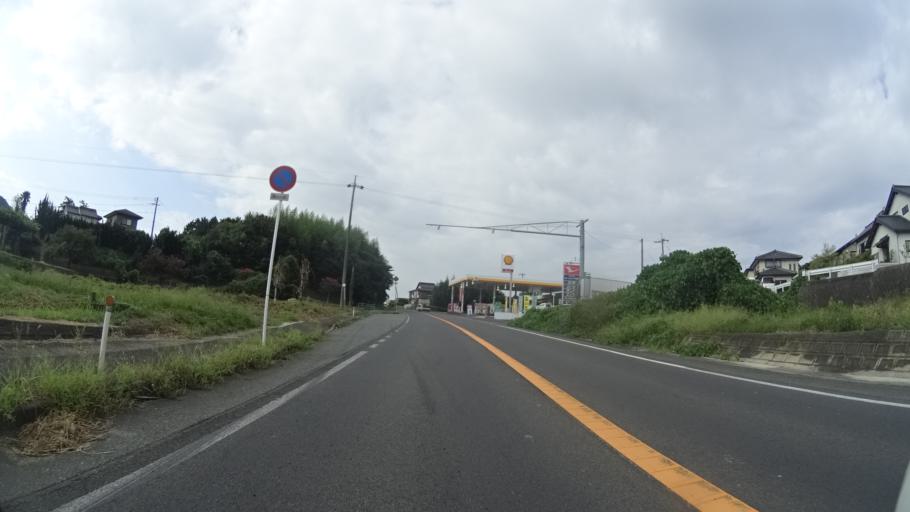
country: JP
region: Shimane
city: Odacho-oda
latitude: 35.2192
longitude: 132.5096
